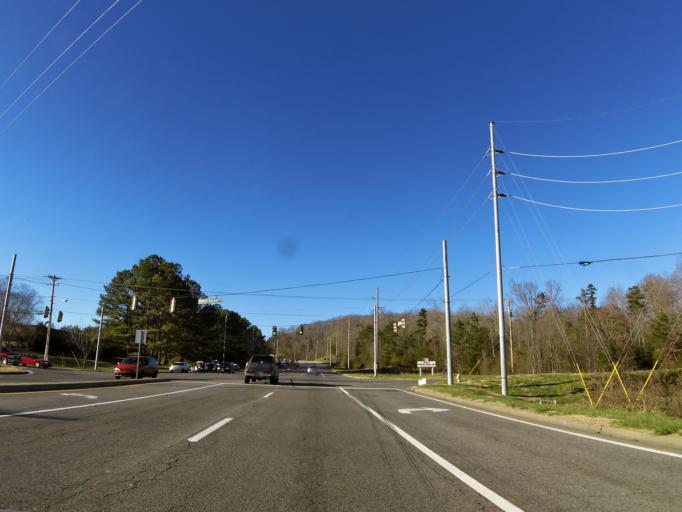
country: US
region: Tennessee
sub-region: Anderson County
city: Oak Ridge
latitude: 35.9991
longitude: -84.2257
